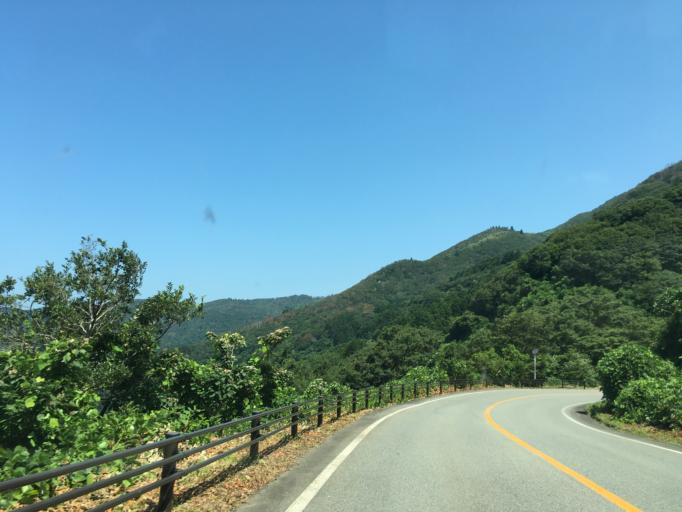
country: JP
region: Akita
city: Tenno
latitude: 39.9006
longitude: 139.7381
